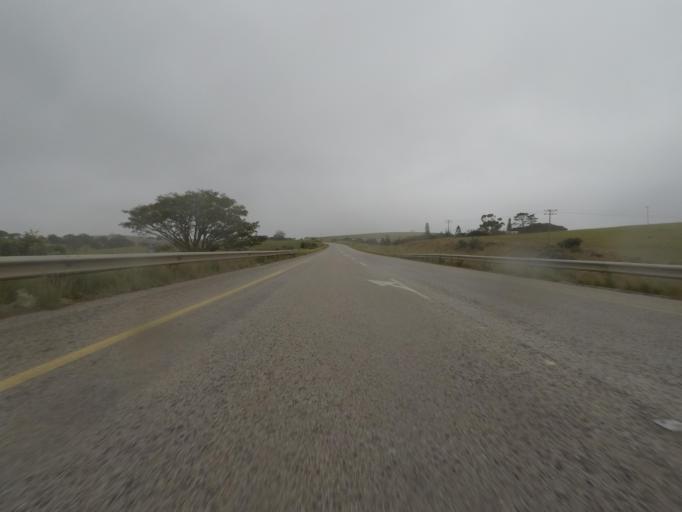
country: ZA
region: Eastern Cape
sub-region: Cacadu District Municipality
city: Grahamstown
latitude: -33.6344
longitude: 26.3178
